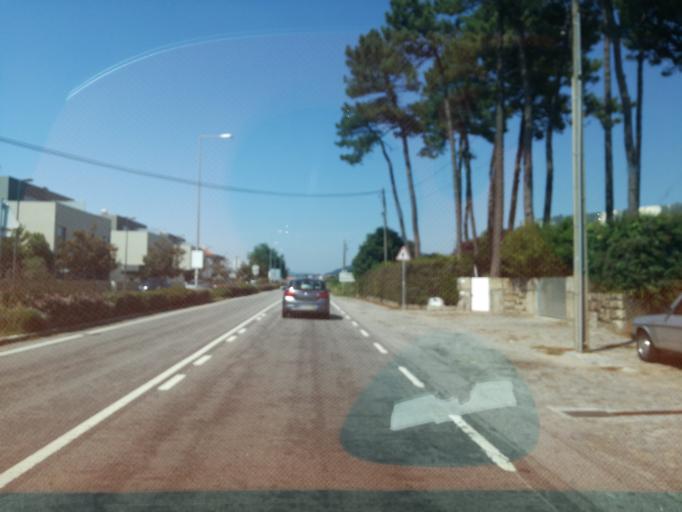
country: PT
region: Braga
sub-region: Esposende
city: Esposende
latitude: 41.5470
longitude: -8.7824
